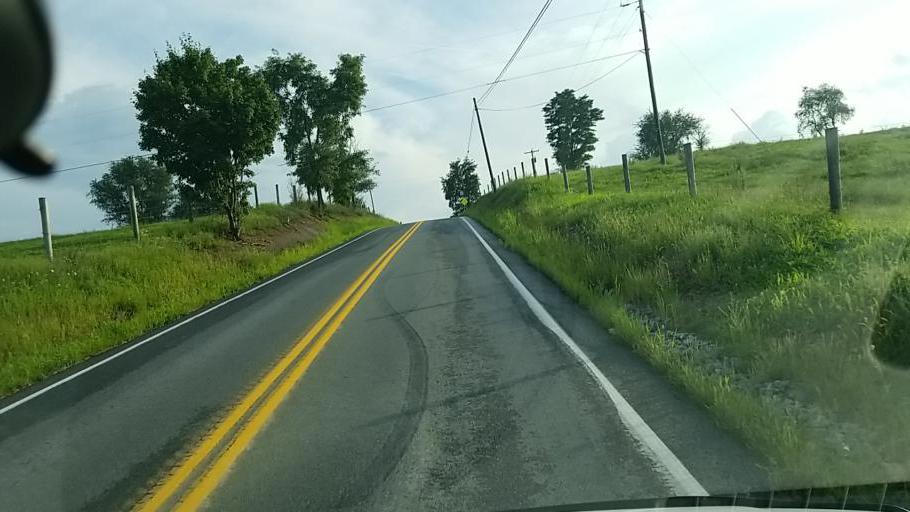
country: US
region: Pennsylvania
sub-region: Cumberland County
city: Newville
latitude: 40.2052
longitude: -77.4756
